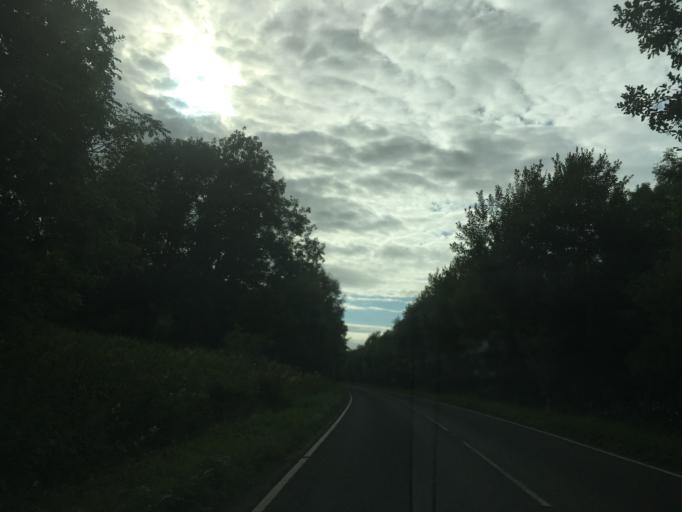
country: GB
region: Scotland
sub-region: Argyll and Bute
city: Oban
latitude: 56.3528
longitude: -5.4838
